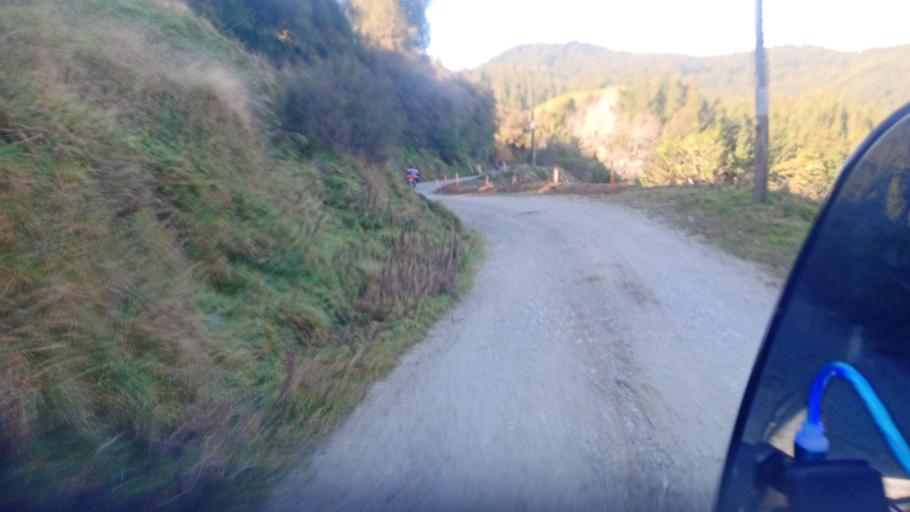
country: NZ
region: Hawke's Bay
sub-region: Wairoa District
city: Wairoa
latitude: -38.6644
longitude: 177.4817
